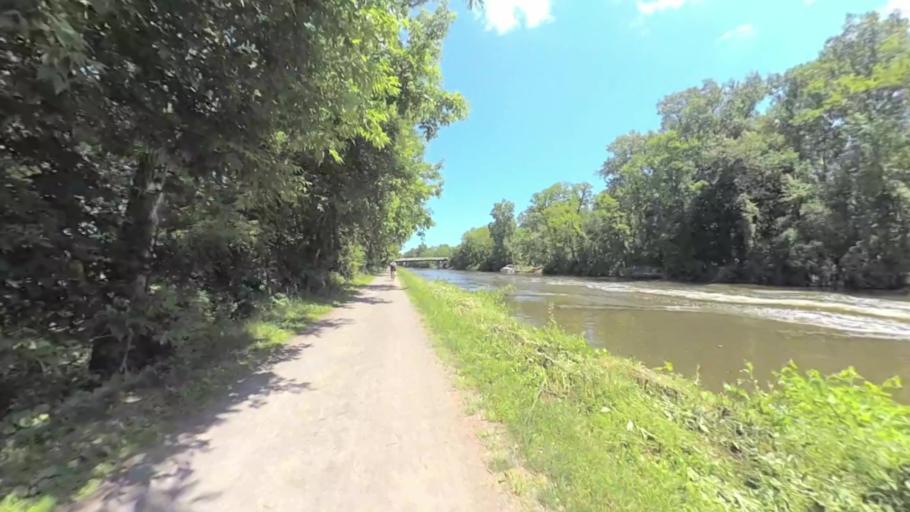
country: US
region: New York
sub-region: Monroe County
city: Fairport
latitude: 43.0776
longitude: -77.4622
